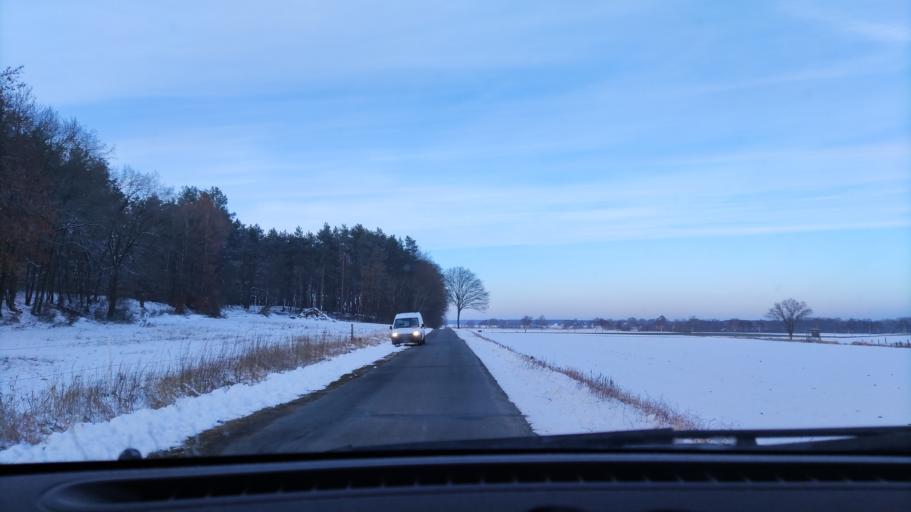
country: DE
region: Lower Saxony
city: Neu Darchau
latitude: 53.2312
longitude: 10.8586
